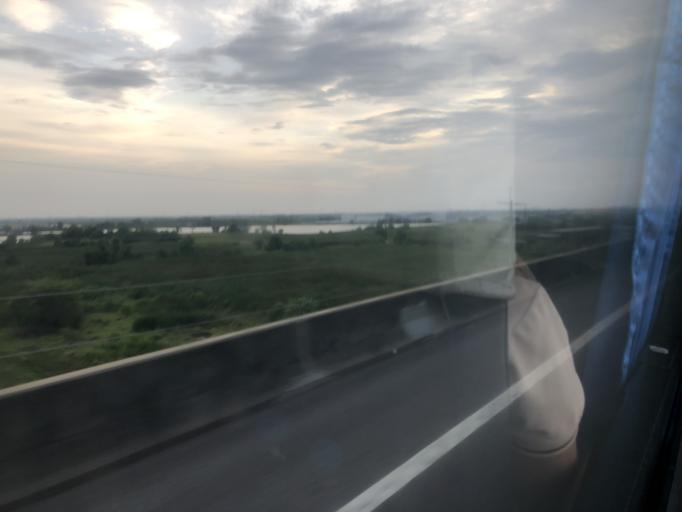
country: TH
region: Samut Prakan
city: Bang Bo
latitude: 13.5792
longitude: 100.8781
